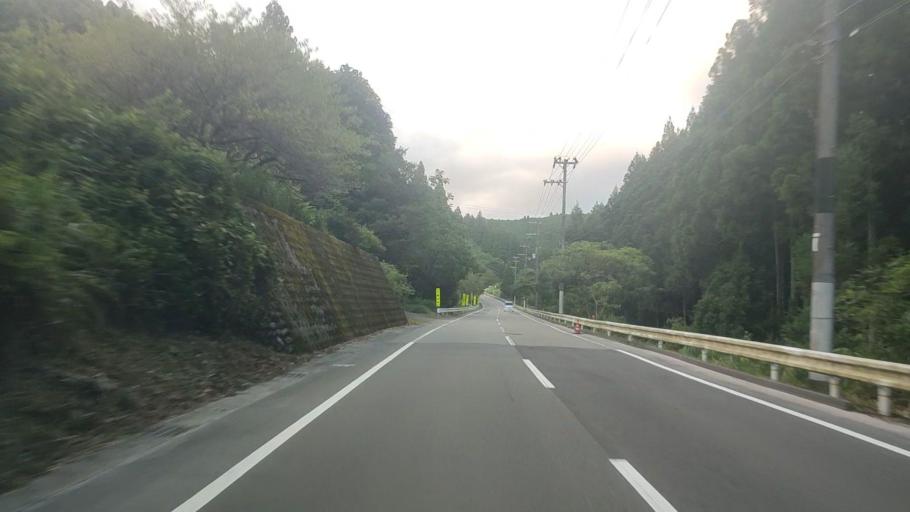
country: JP
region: Wakayama
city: Tanabe
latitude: 33.8296
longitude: 135.6429
